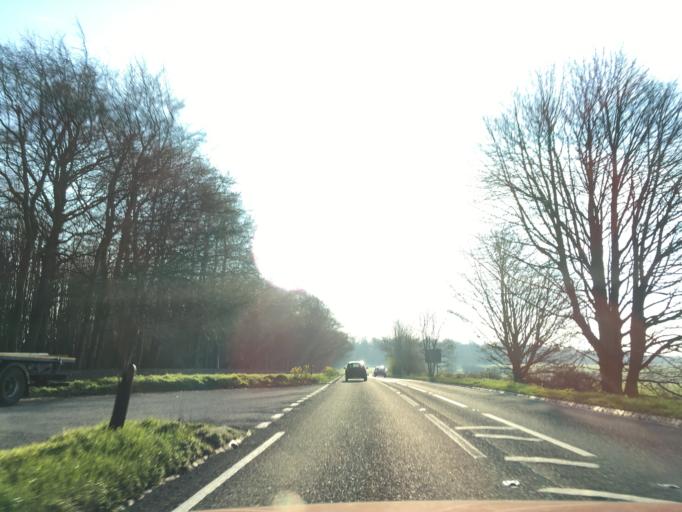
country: GB
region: England
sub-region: Gloucestershire
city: Bourton on the Water
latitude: 51.8225
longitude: -1.7738
